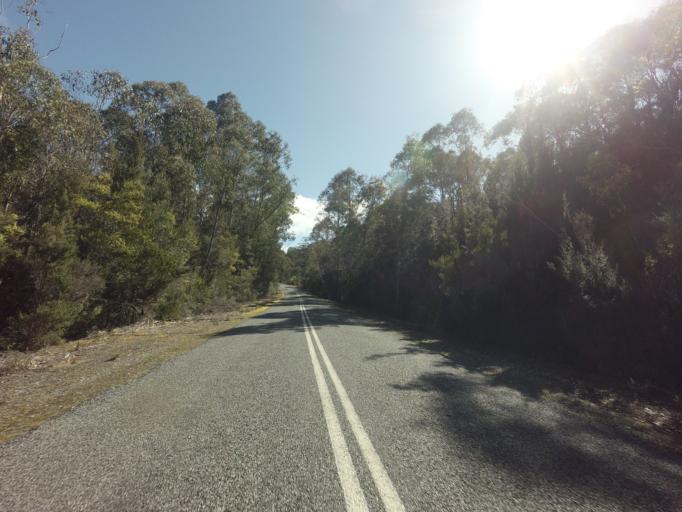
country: AU
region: Tasmania
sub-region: Huon Valley
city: Geeveston
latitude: -42.7652
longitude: 146.3972
